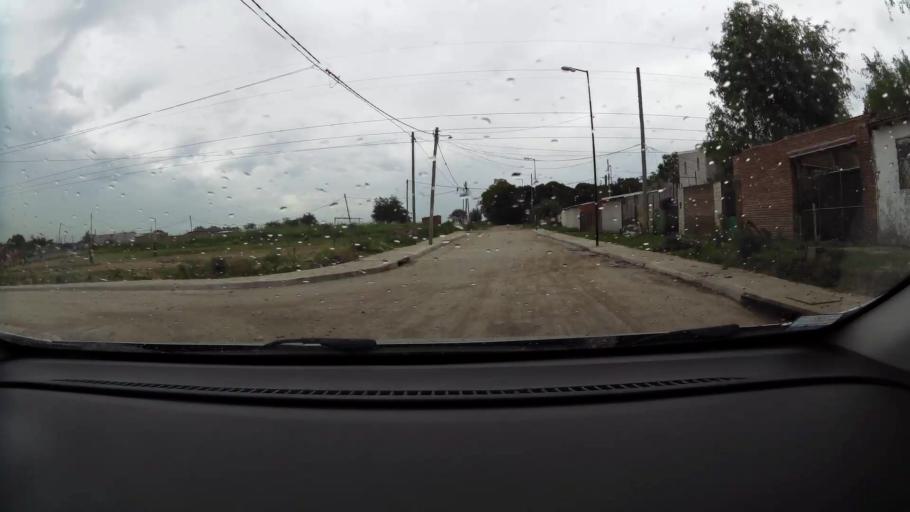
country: AR
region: Buenos Aires
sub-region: Partido de Zarate
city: Zarate
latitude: -34.1179
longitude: -59.0423
